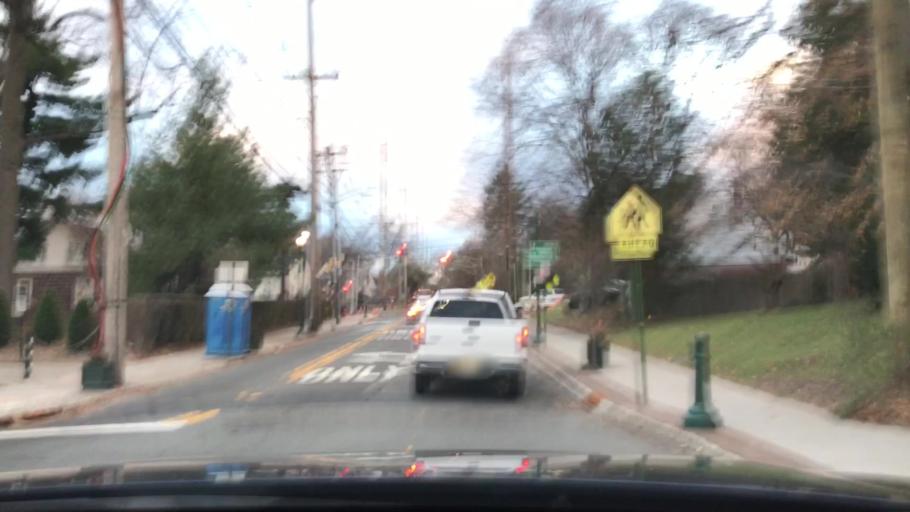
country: US
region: New Jersey
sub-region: Bergen County
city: Maywood
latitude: 40.8960
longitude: -74.0655
